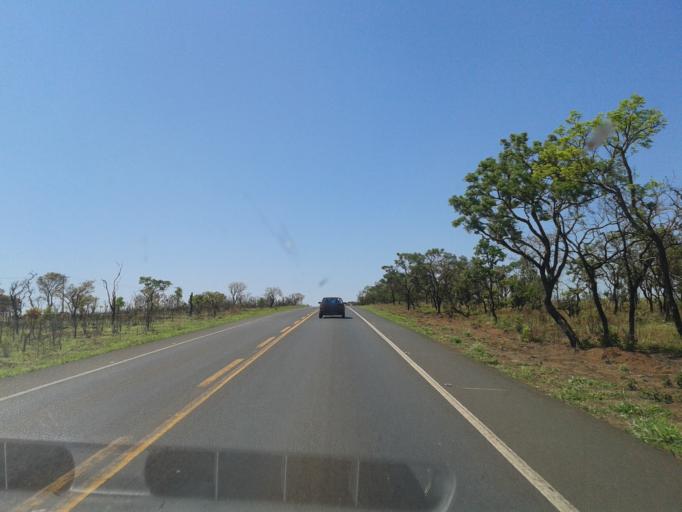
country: BR
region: Minas Gerais
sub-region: Uberaba
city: Uberaba
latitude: -19.3001
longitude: -47.5909
